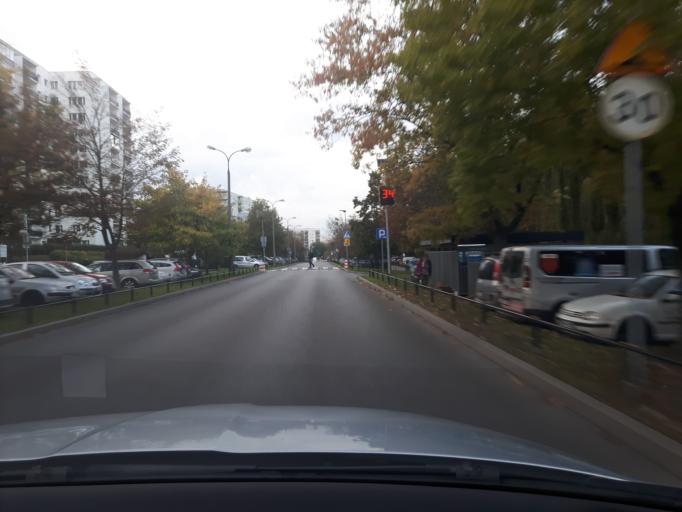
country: PL
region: Masovian Voivodeship
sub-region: Warszawa
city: Ursynow
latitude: 52.1405
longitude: 21.0518
